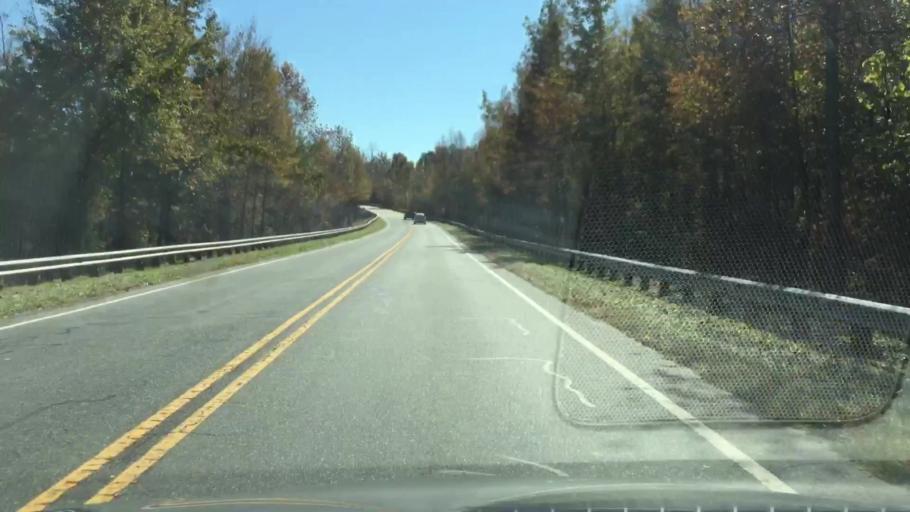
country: US
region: North Carolina
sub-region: Rockingham County
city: Reidsville
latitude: 36.2673
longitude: -79.6523
